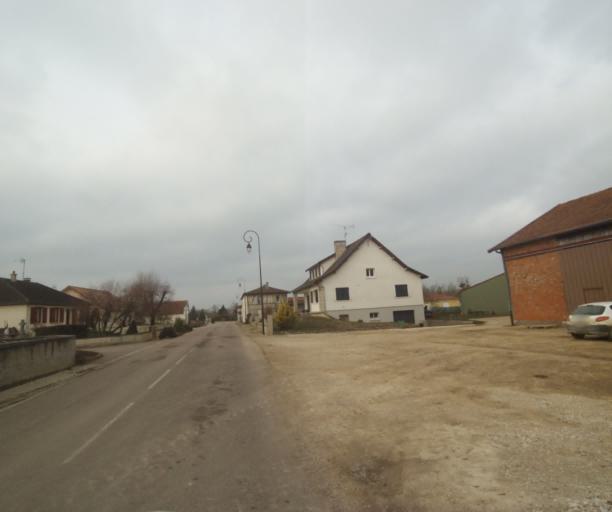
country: FR
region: Champagne-Ardenne
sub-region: Departement de la Haute-Marne
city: Villiers-en-Lieu
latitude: 48.6507
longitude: 4.8122
